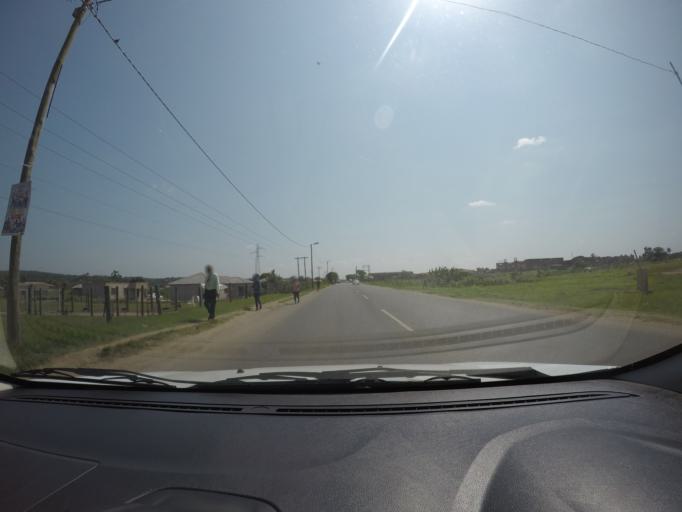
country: ZA
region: KwaZulu-Natal
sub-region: uThungulu District Municipality
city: eSikhawini
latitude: -28.8676
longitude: 31.9057
